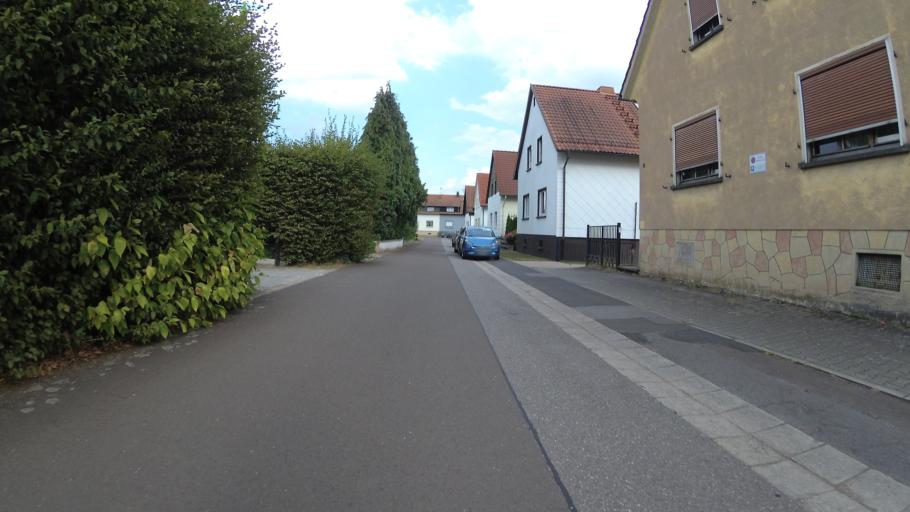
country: DE
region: Saarland
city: Bexbach
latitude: 49.3161
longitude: 7.2647
